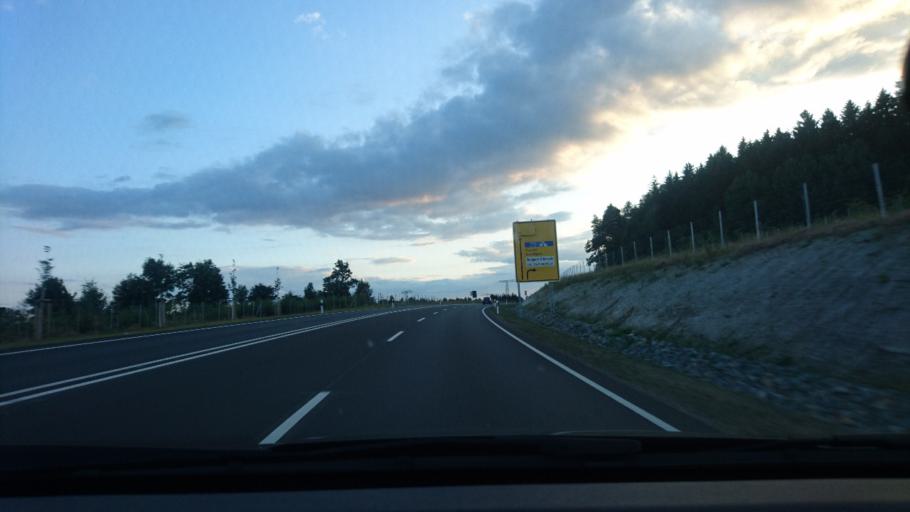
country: DE
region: Saxony
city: Auerbach
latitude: 50.5282
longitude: 12.3869
